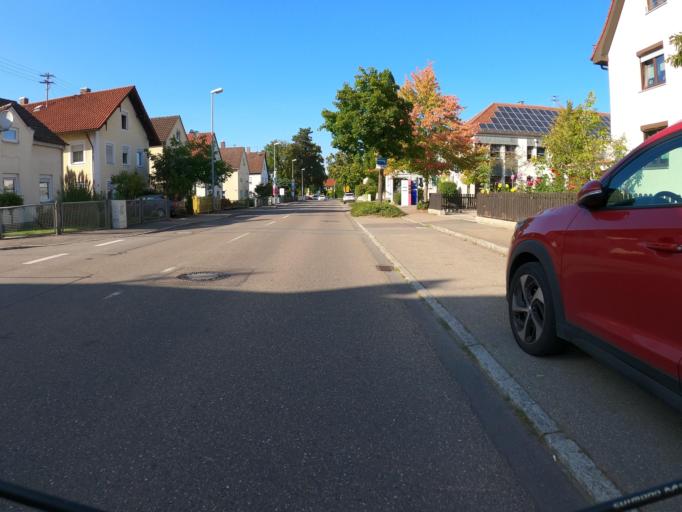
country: DE
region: Bavaria
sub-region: Swabia
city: Weissenhorn
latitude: 48.3075
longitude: 10.1599
